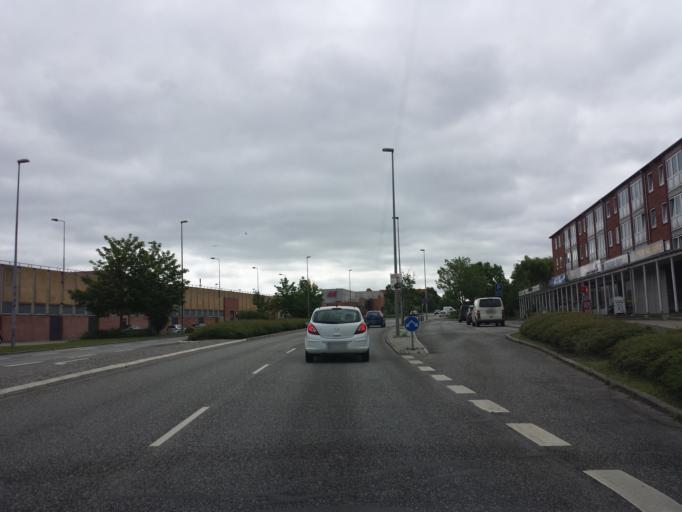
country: DK
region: Capital Region
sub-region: Ballerup Kommune
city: Ballerup
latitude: 55.7287
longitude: 12.3556
